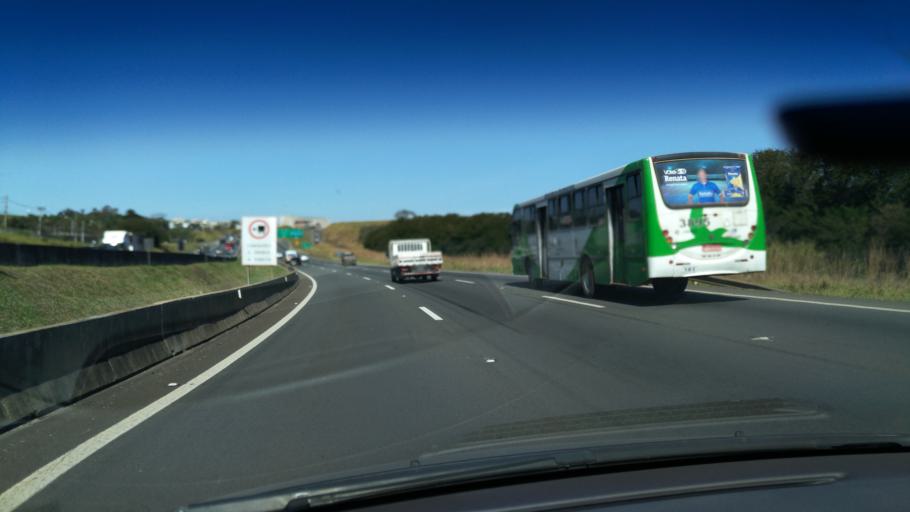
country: BR
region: Sao Paulo
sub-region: Campinas
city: Campinas
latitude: -22.8240
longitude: -47.0371
